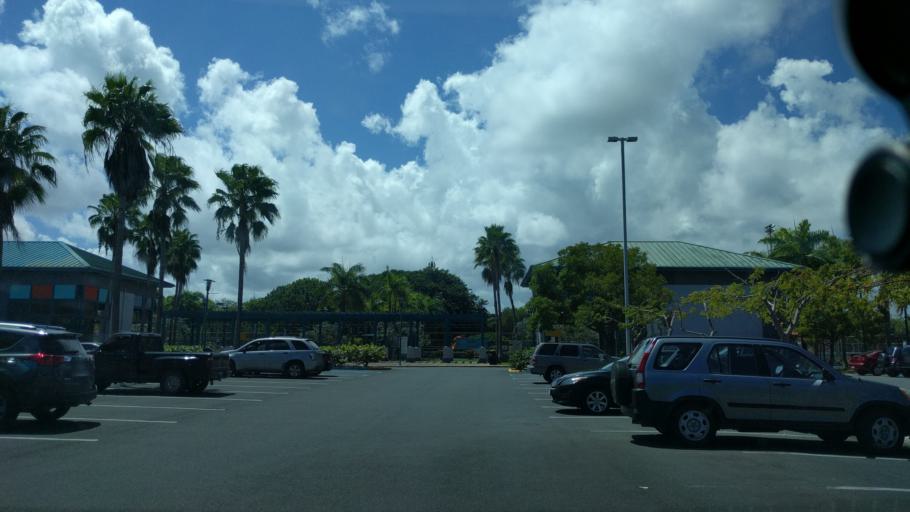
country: PR
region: San Juan
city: San Juan
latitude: 18.4417
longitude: -66.0785
